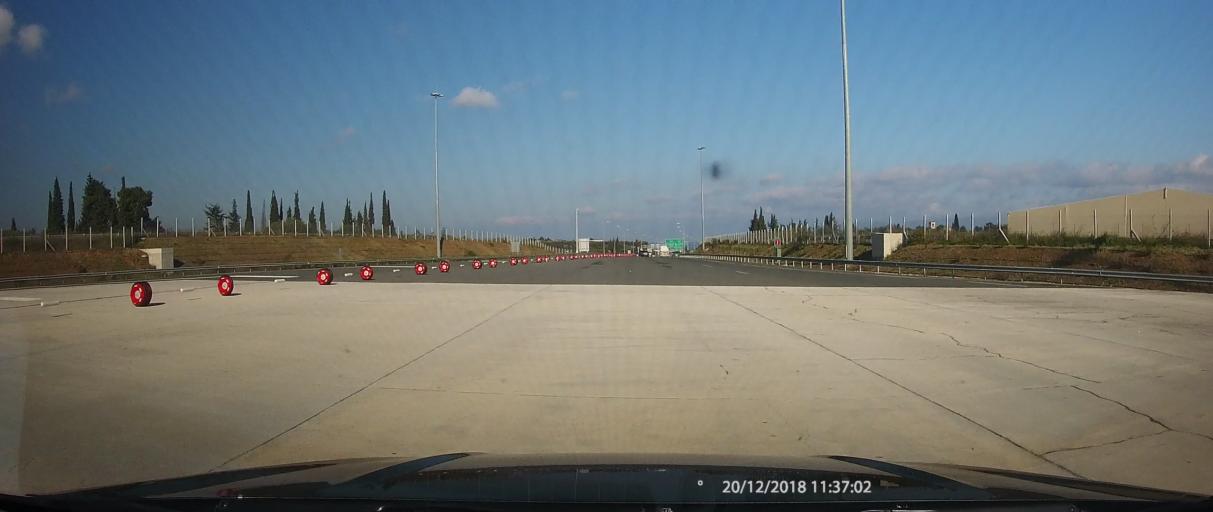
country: GR
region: Peloponnese
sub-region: Nomos Korinthias
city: Moulki
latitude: 37.9974
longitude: 22.7357
